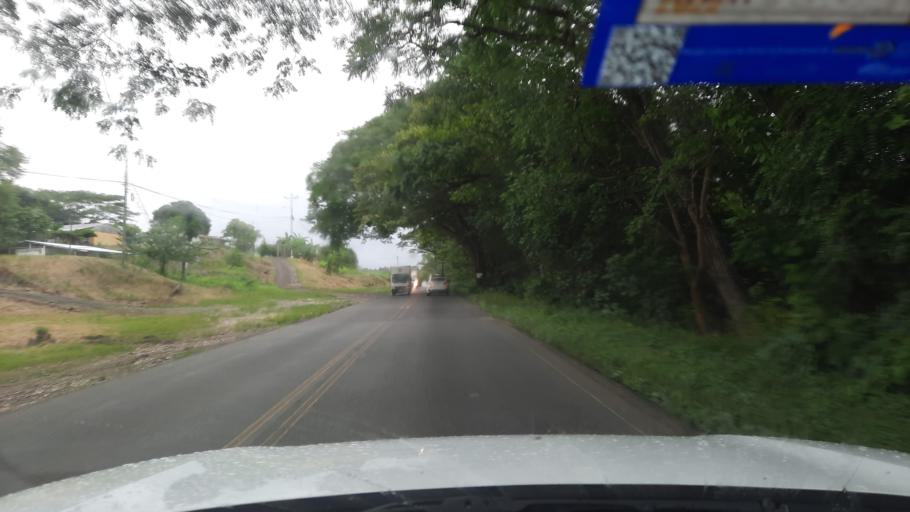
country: CR
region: Guanacaste
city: Juntas
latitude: 10.1324
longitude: -84.9034
